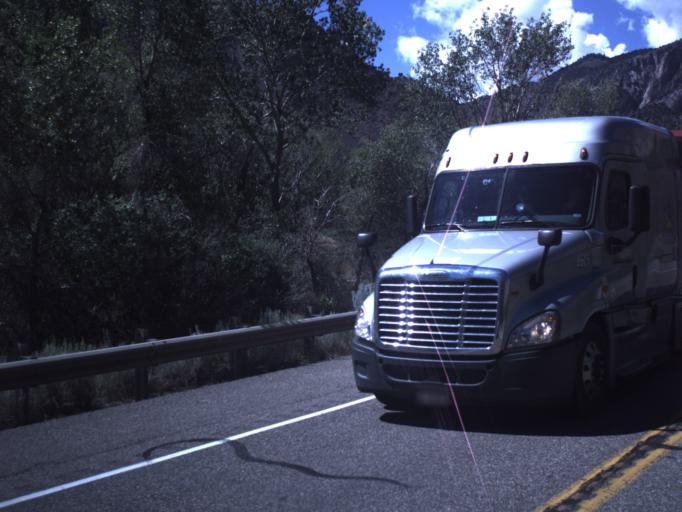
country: US
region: Utah
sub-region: Sevier County
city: Monroe
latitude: 38.5688
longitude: -112.2669
